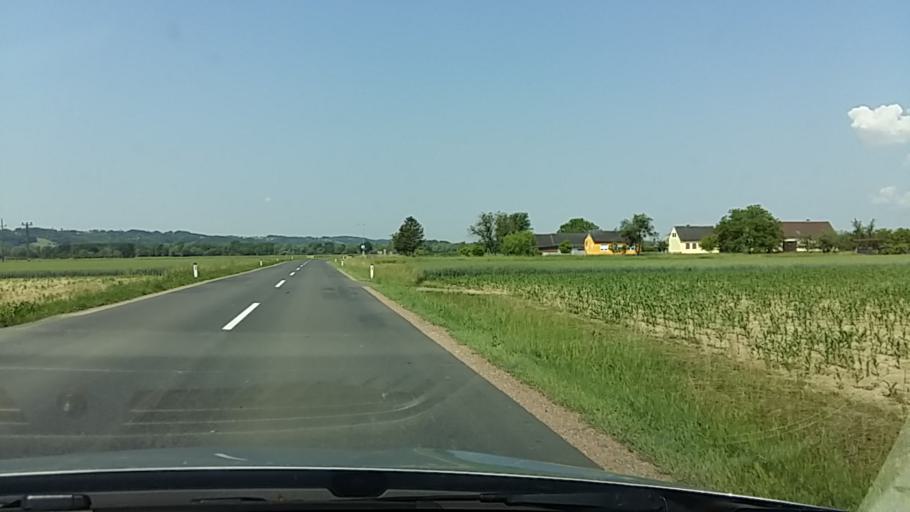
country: AT
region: Burgenland
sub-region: Politischer Bezirk Jennersdorf
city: Heiligenkreuz im Lafnitztal
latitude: 46.9828
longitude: 16.2600
